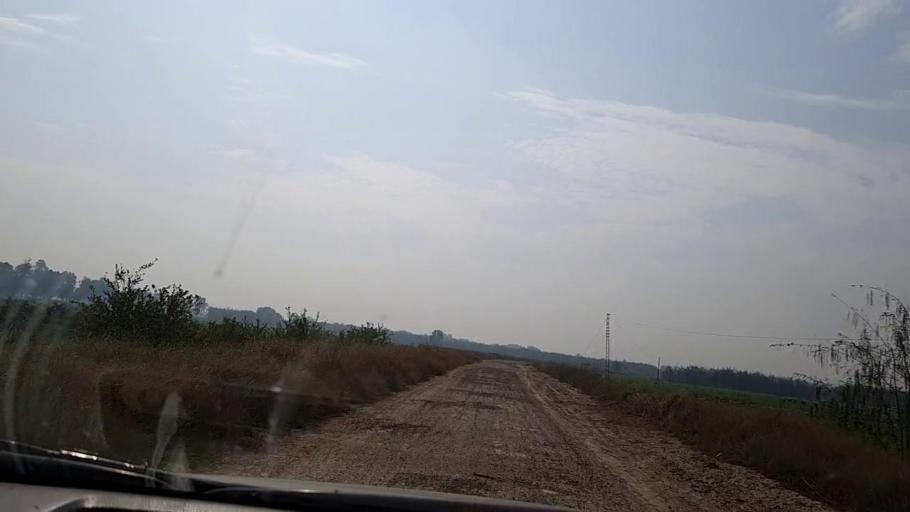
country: PK
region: Sindh
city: Daulatpur
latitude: 26.5328
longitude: 67.9825
